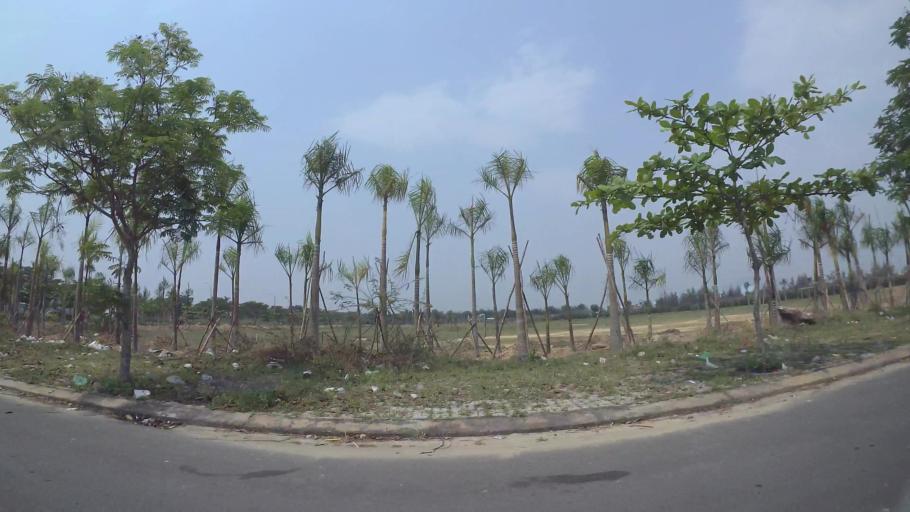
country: VN
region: Da Nang
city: Cam Le
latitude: 15.9952
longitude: 108.2105
